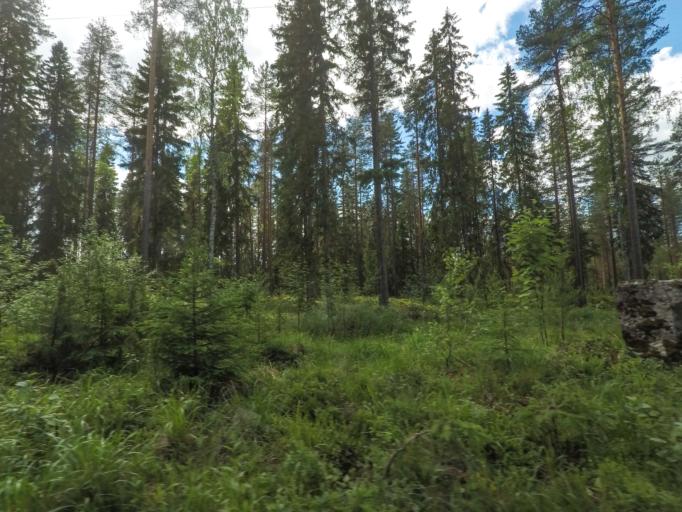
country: FI
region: Central Finland
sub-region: Jyvaeskylae
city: Hankasalmi
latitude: 62.4079
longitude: 26.6516
